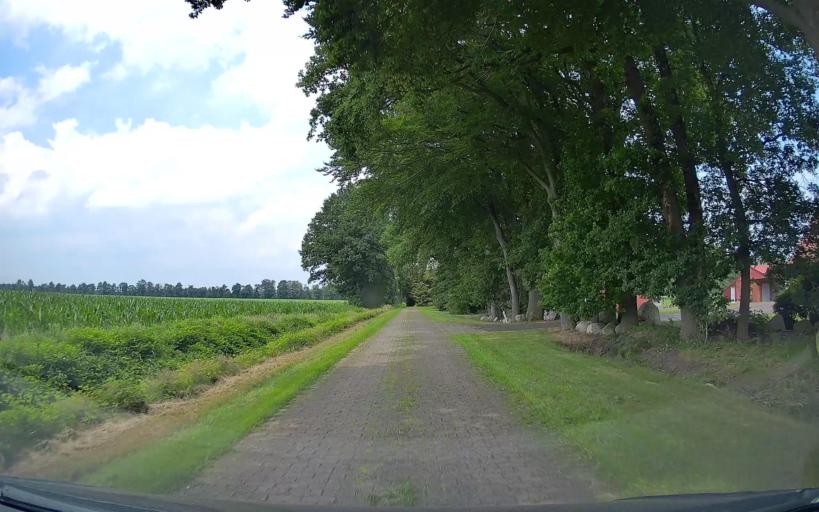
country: DE
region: Lower Saxony
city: Bosel
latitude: 52.9937
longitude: 7.9013
